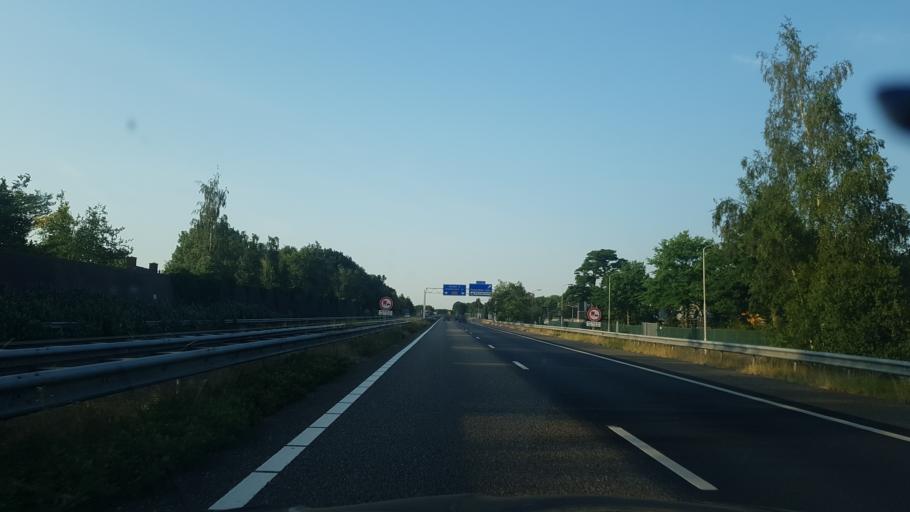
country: NL
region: North Brabant
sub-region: Roosendaal
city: Roosendaal
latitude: 51.5288
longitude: 4.4759
